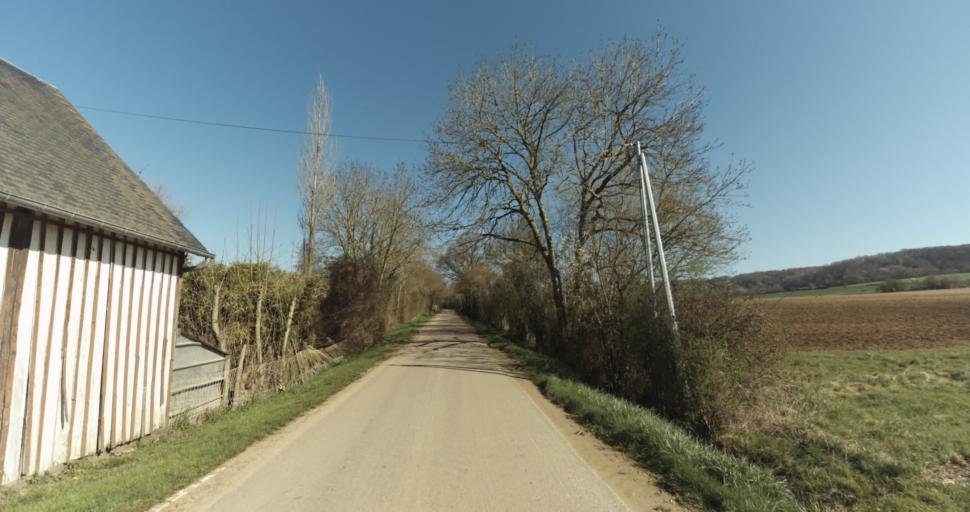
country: FR
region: Lower Normandy
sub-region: Departement du Calvados
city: Saint-Pierre-sur-Dives
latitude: 48.9690
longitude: 0.0519
